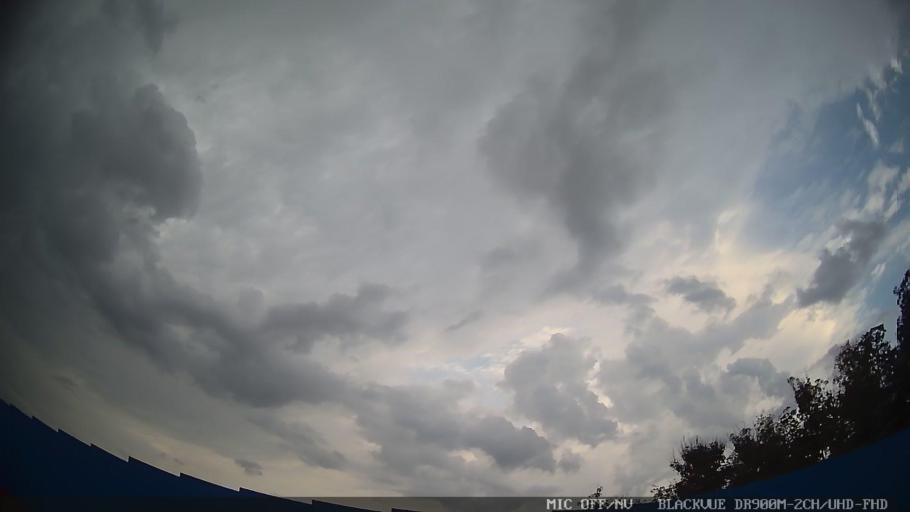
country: BR
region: Sao Paulo
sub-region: Itatiba
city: Itatiba
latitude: -23.0013
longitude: -46.8601
